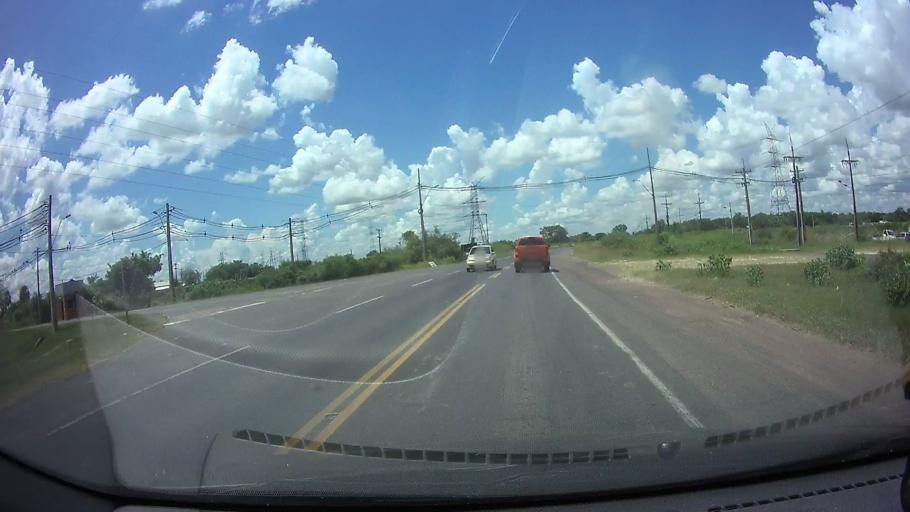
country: PY
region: Central
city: Colonia Mariano Roque Alonso
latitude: -25.1786
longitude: -57.5853
